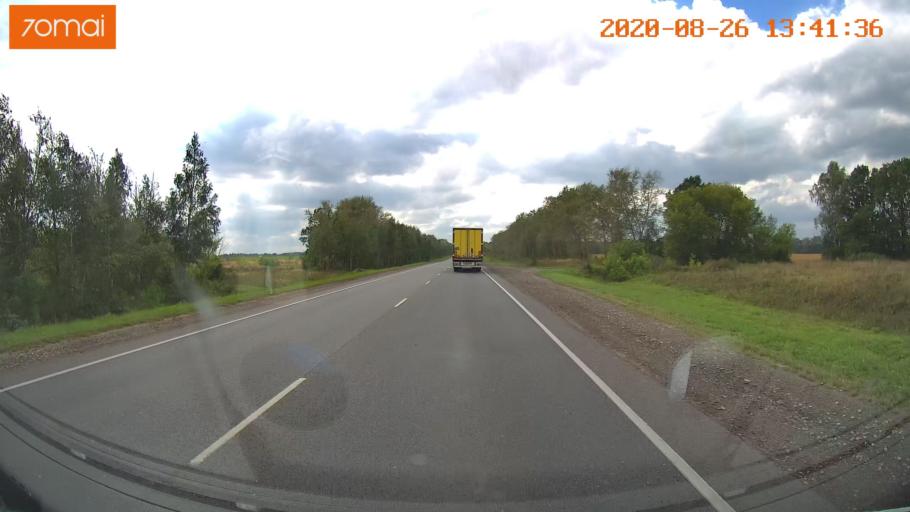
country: RU
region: Rjazan
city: Ryazan'
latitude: 54.5812
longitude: 39.5892
